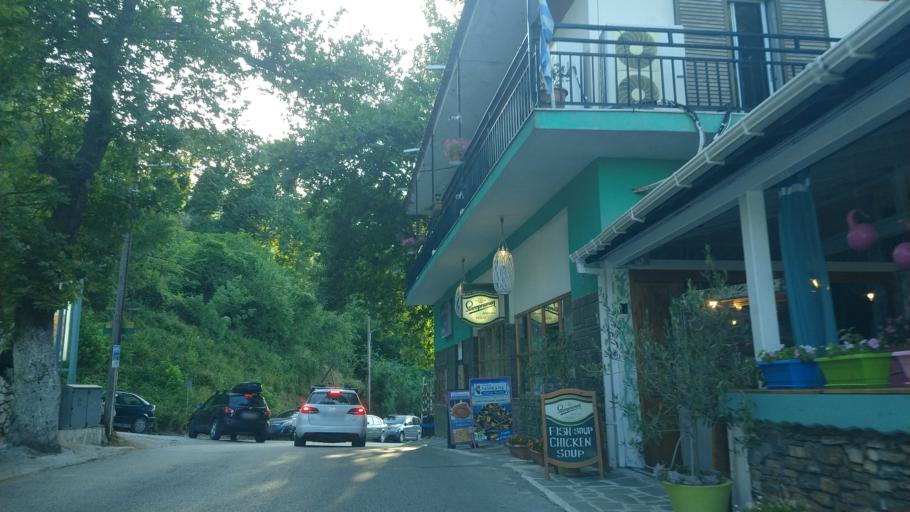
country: GR
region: East Macedonia and Thrace
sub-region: Nomos Kavalas
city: Potamia
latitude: 40.7295
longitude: 24.7315
